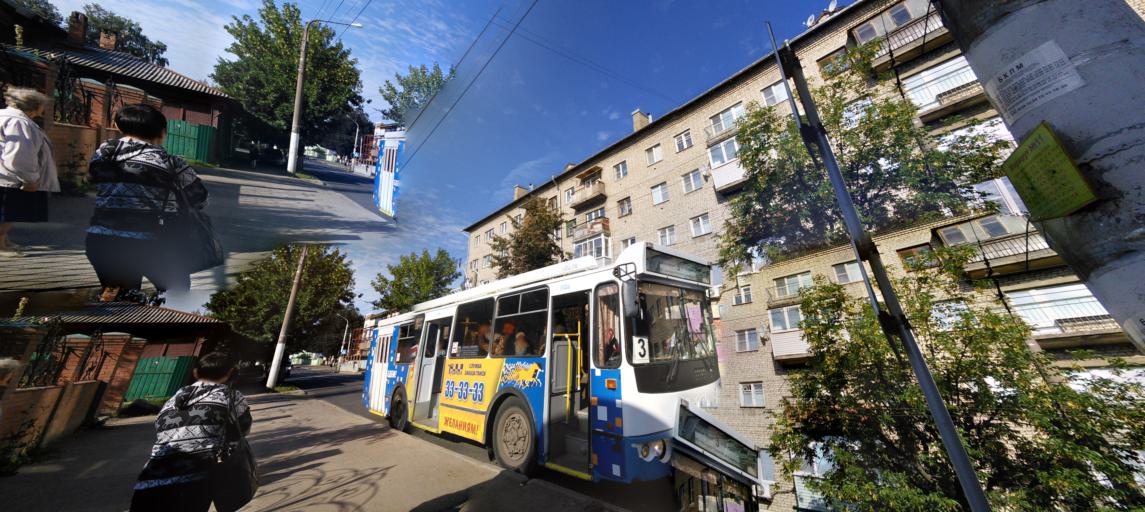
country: RU
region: Kostroma
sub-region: Kostromskoy Rayon
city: Kostroma
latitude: 57.7784
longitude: 40.9120
